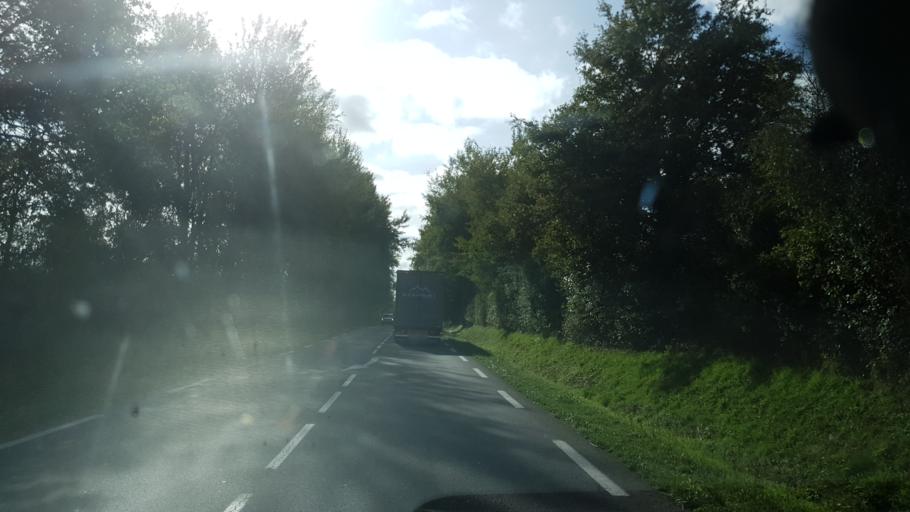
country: FR
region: Poitou-Charentes
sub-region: Departement de la Charente
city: Confolens
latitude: 46.0448
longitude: 0.6636
